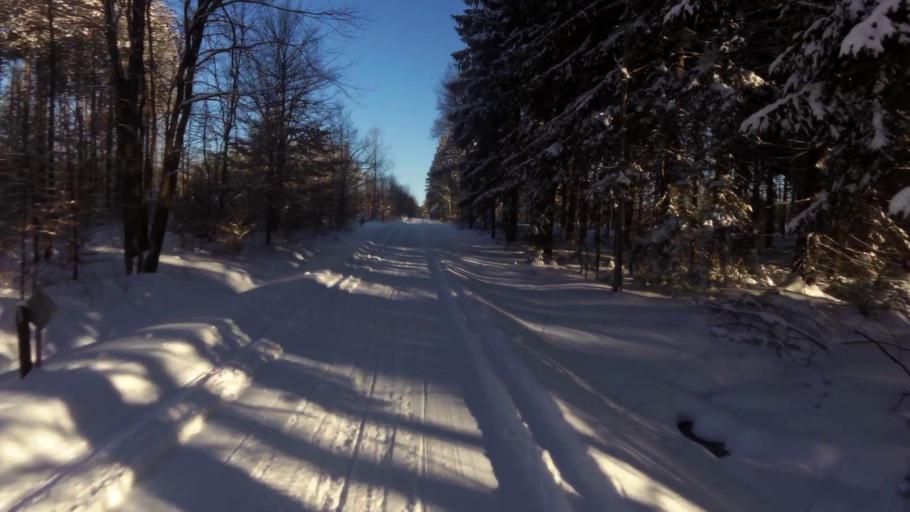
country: US
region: New York
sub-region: Chautauqua County
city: Falconer
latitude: 42.2418
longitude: -79.2131
